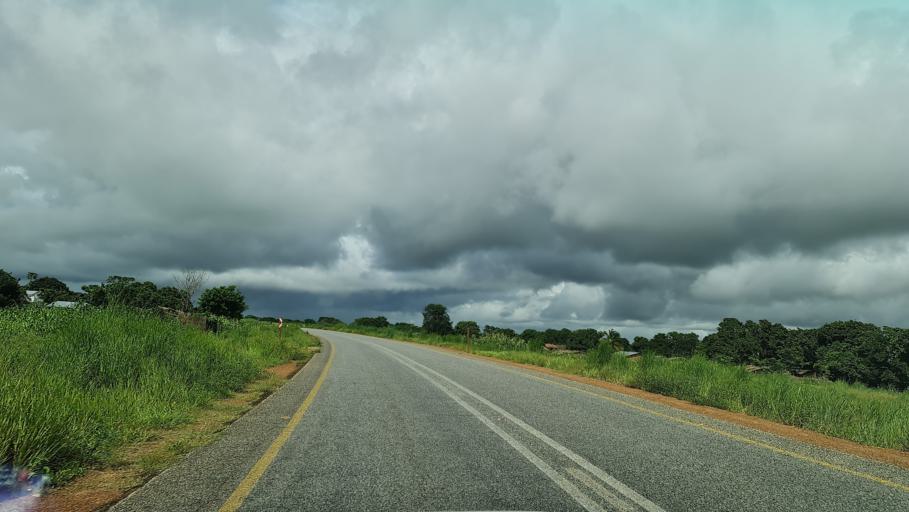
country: MZ
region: Nampula
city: Nampula
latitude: -15.0341
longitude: 38.4312
